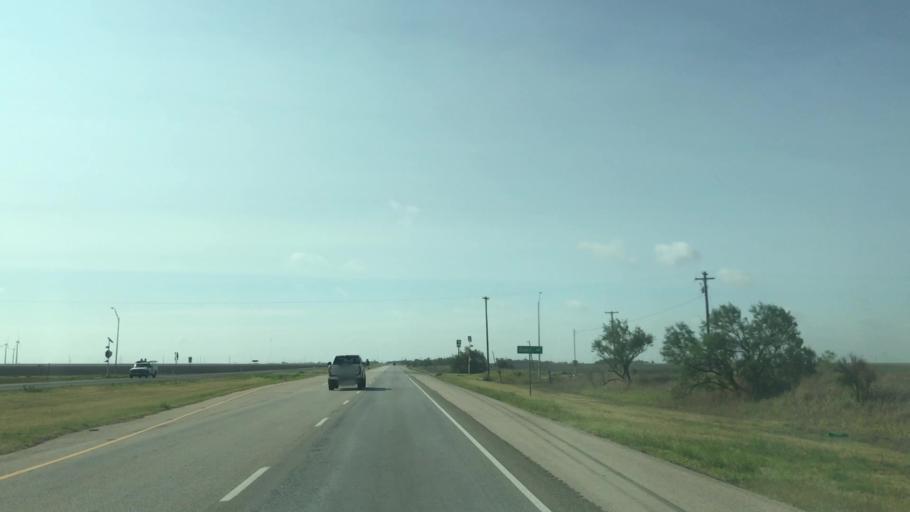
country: US
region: Texas
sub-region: Scurry County
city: Snyder
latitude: 32.5892
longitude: -100.7312
